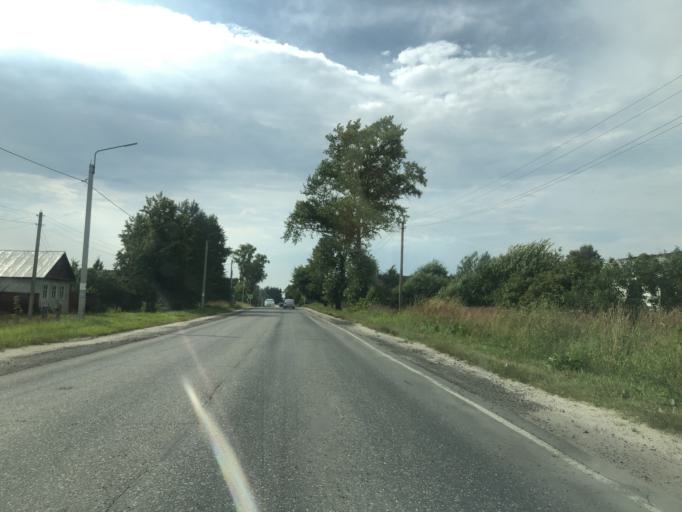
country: RU
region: Ivanovo
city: Shuya
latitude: 56.8569
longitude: 41.5082
